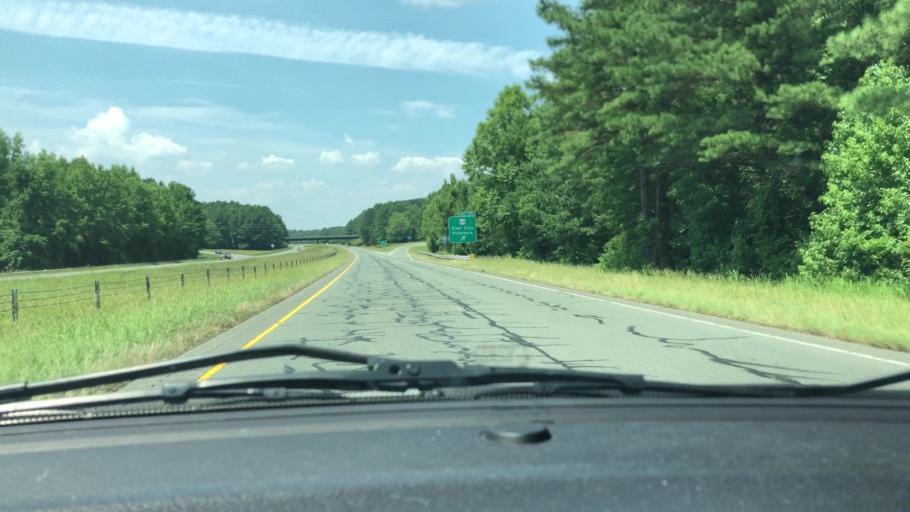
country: US
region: North Carolina
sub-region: Chatham County
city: Siler City
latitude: 35.7286
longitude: -79.4303
